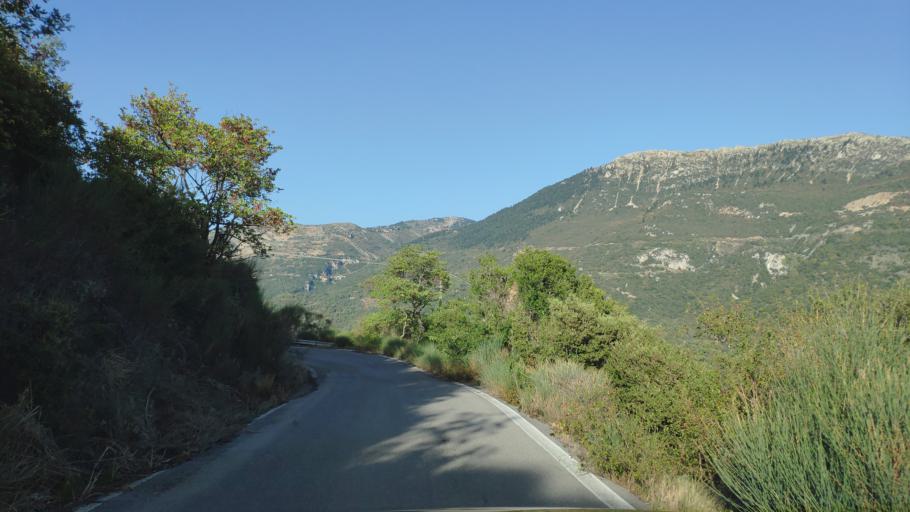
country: GR
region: Peloponnese
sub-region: Nomos Arkadias
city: Dimitsana
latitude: 37.5561
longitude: 22.0401
